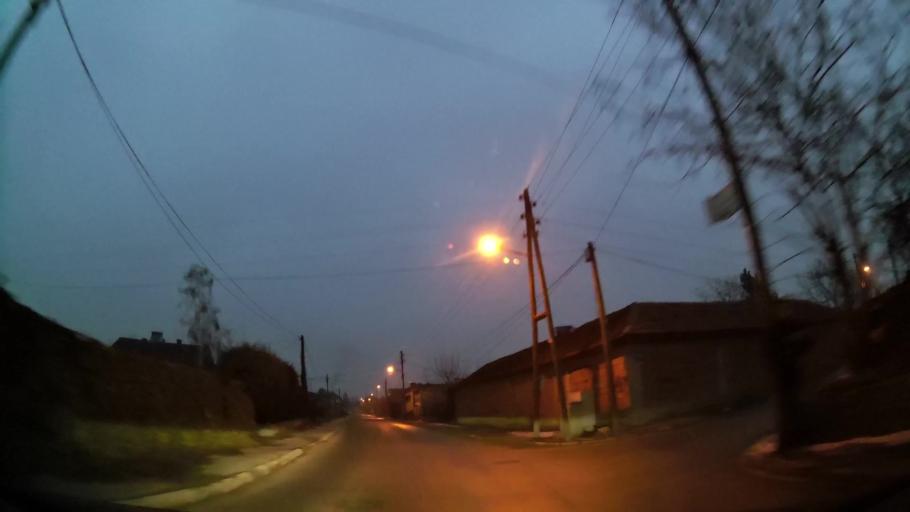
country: MK
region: Kisela Voda
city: Kisela Voda
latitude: 41.9662
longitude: 21.4870
